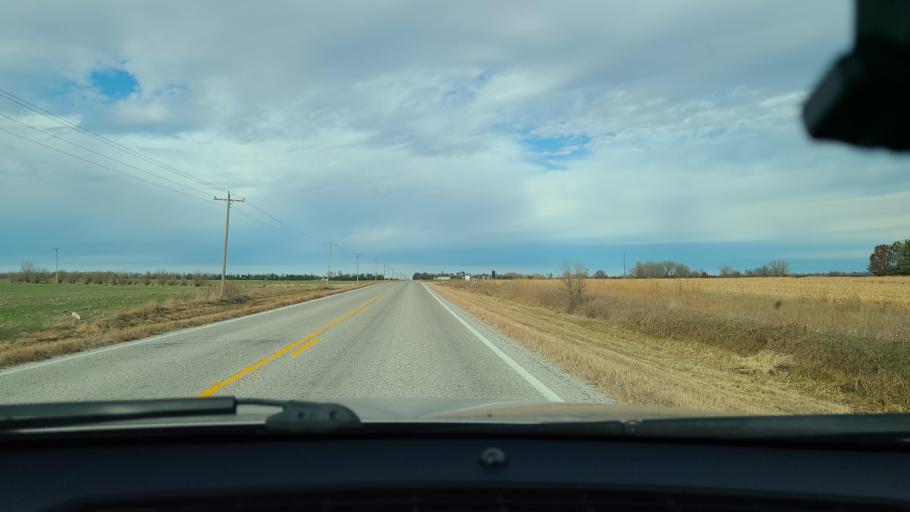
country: US
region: Kansas
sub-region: McPherson County
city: Inman
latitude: 38.3021
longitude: -97.9249
